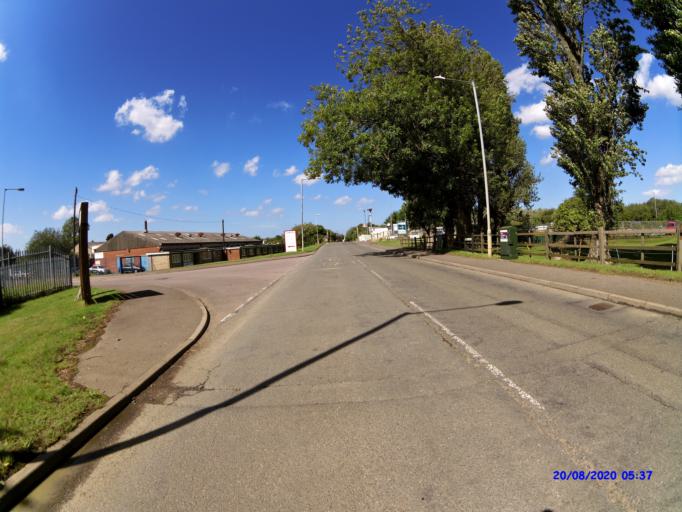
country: GB
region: England
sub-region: Cambridgeshire
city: Whittlesey
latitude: 52.5490
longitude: -0.1190
